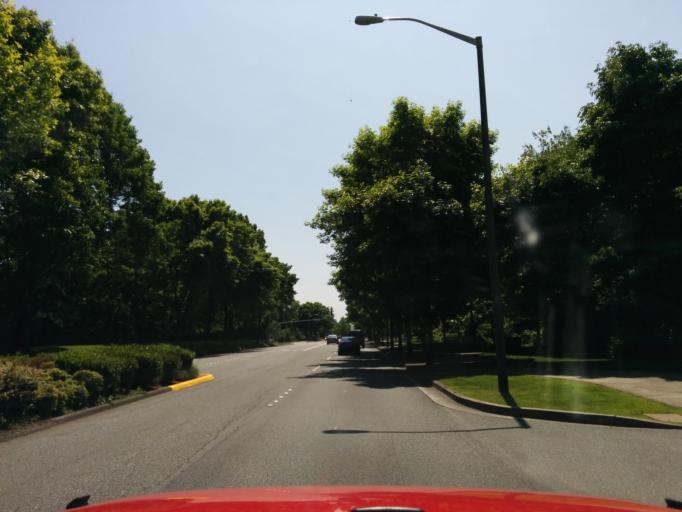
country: US
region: Washington
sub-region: King County
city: Redmond
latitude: 47.6398
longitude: -122.1325
